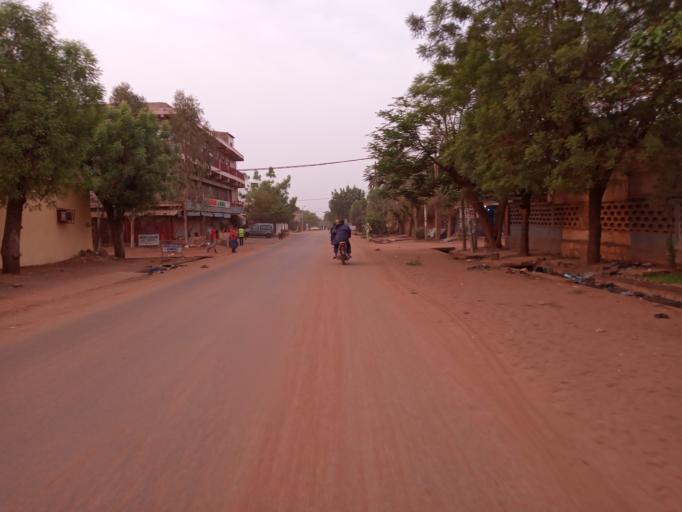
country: ML
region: Bamako
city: Bamako
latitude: 12.6648
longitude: -7.9735
